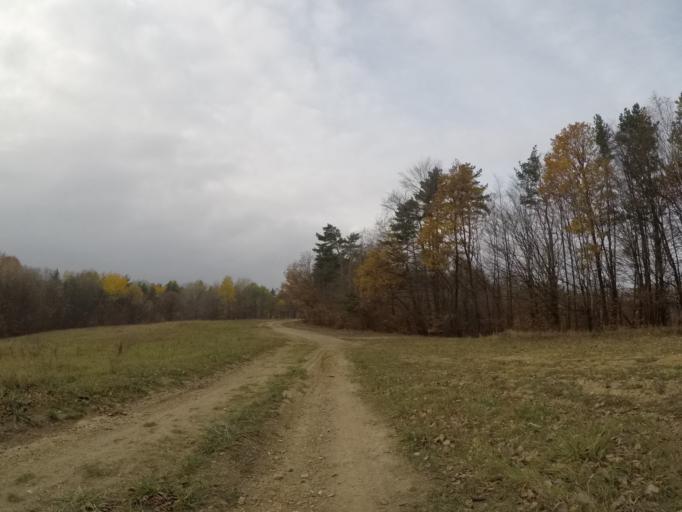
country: SK
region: Presovsky
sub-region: Okres Presov
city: Presov
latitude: 48.9356
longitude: 21.1255
